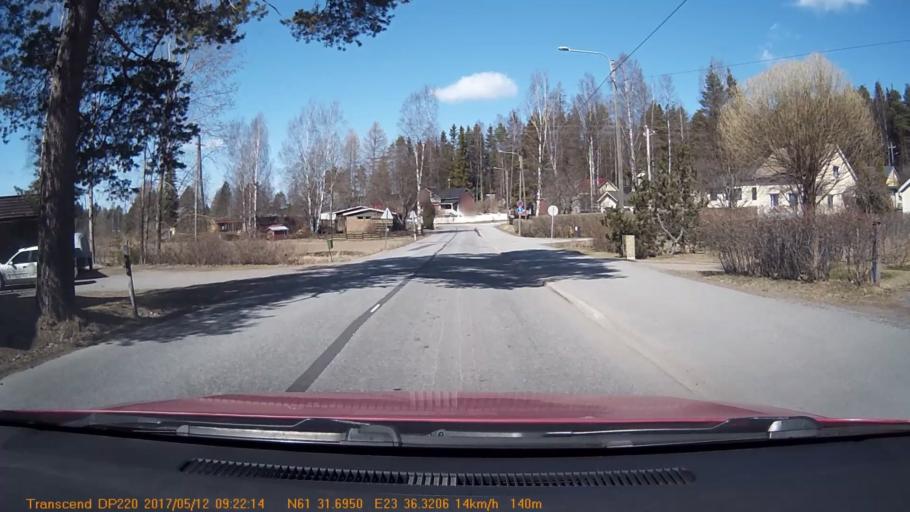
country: FI
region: Pirkanmaa
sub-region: Tampere
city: Yloejaervi
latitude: 61.5282
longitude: 23.6053
